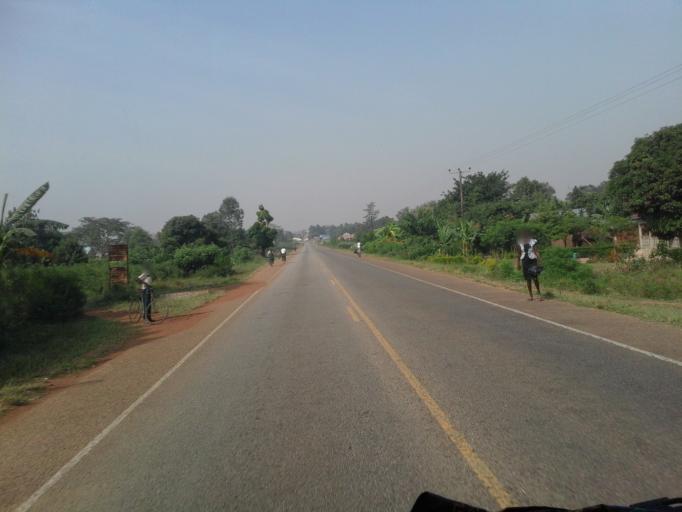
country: UG
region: Eastern Region
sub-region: Budaka District
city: Budaka
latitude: 1.0217
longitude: 33.9701
